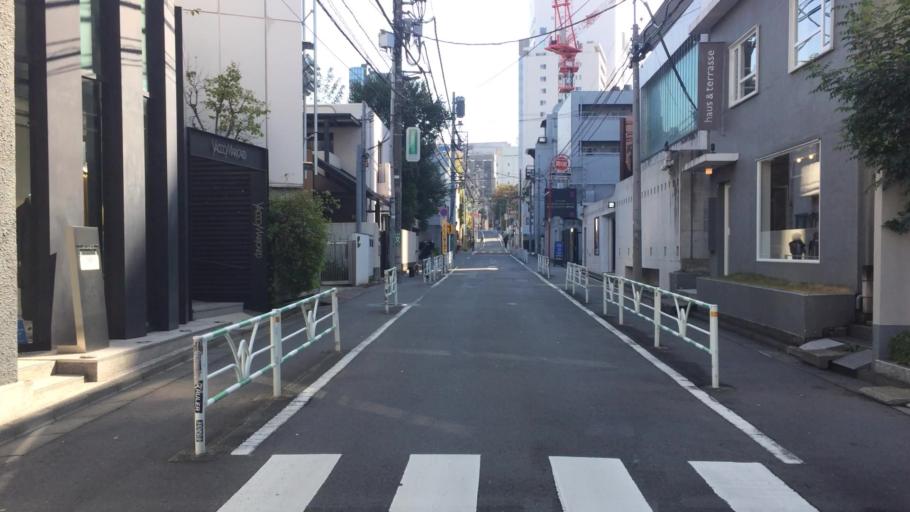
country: JP
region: Tokyo
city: Tokyo
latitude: 35.6635
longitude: 139.7043
